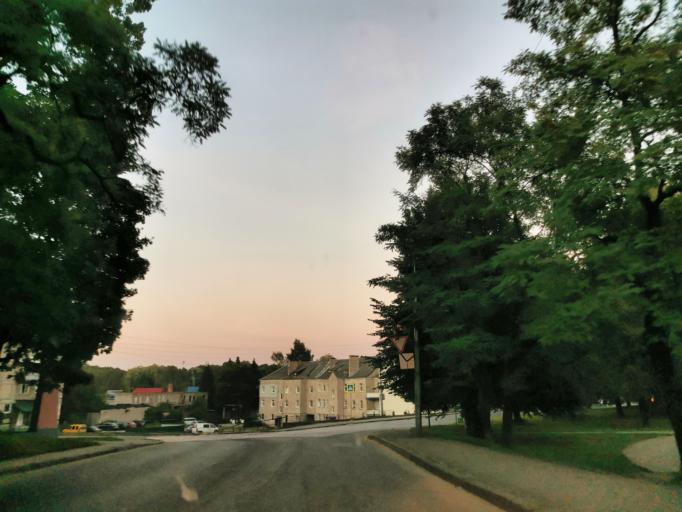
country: RU
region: Kaliningrad
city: Chernyakhovsk
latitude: 54.6393
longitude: 21.8070
